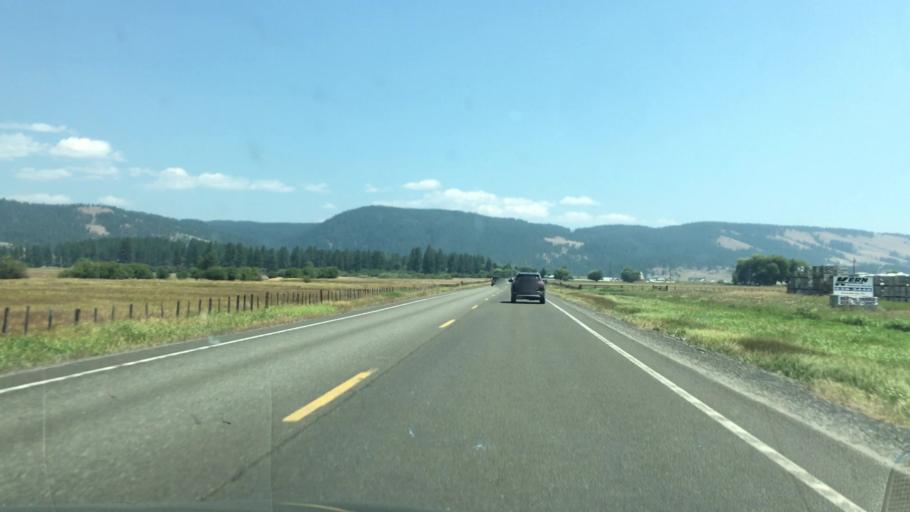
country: US
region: Idaho
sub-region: Valley County
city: McCall
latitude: 44.9670
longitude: -116.2676
